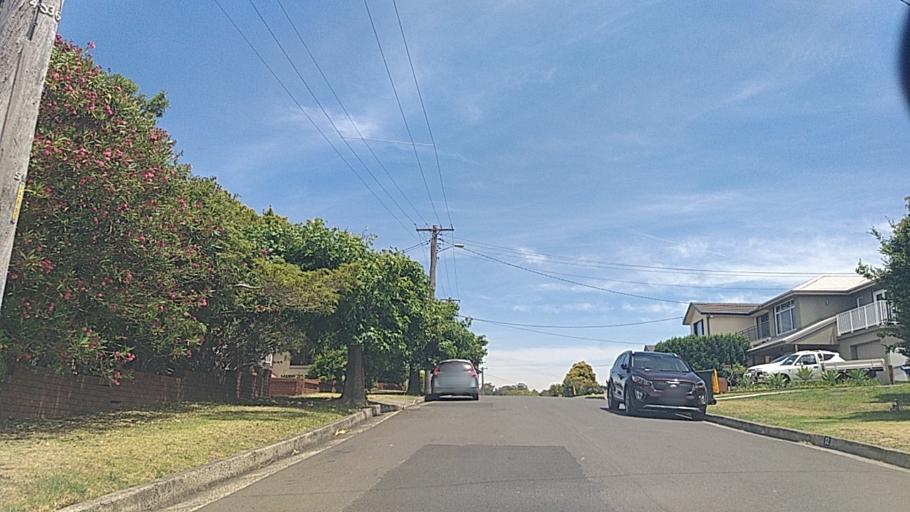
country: AU
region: New South Wales
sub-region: Wollongong
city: Mount Ousley
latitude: -34.3911
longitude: 150.8830
